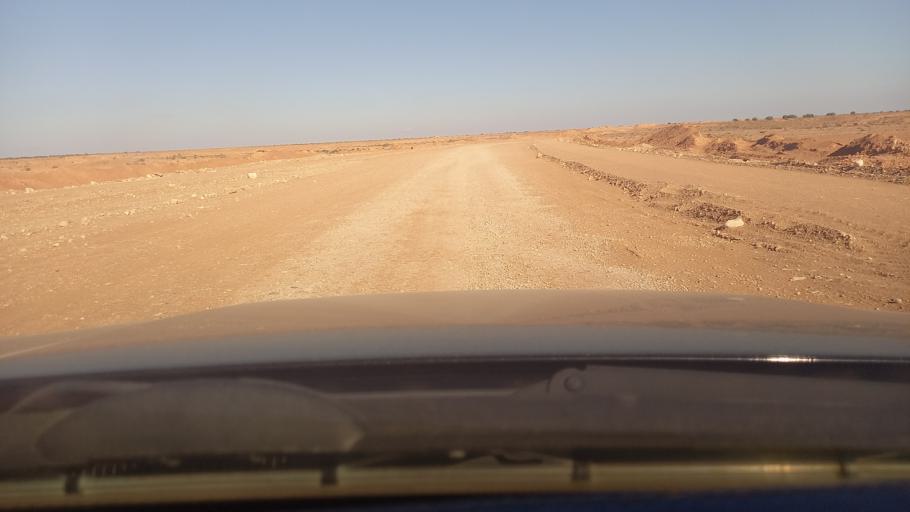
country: TN
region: Madanin
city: Medenine
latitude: 33.1448
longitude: 10.5065
